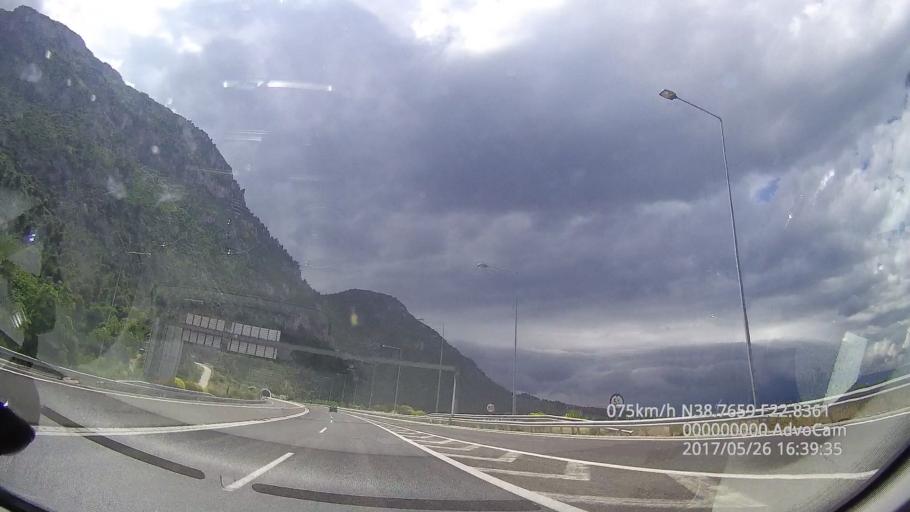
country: GR
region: Central Greece
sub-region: Nomos Fthiotidos
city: Rodhitsa
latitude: 38.9042
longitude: 22.5240
